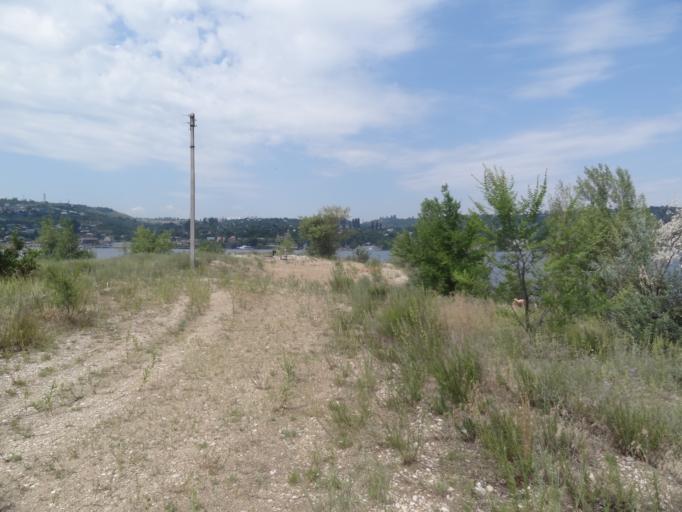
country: RU
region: Saratov
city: Engel's
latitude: 51.5412
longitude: 46.0907
